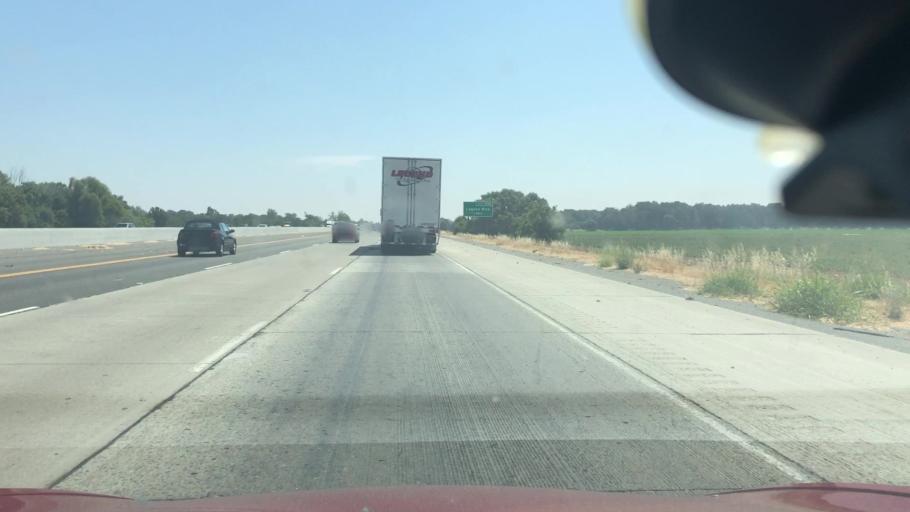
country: US
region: California
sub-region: Sacramento County
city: Parkway
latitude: 38.4470
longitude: -121.4919
